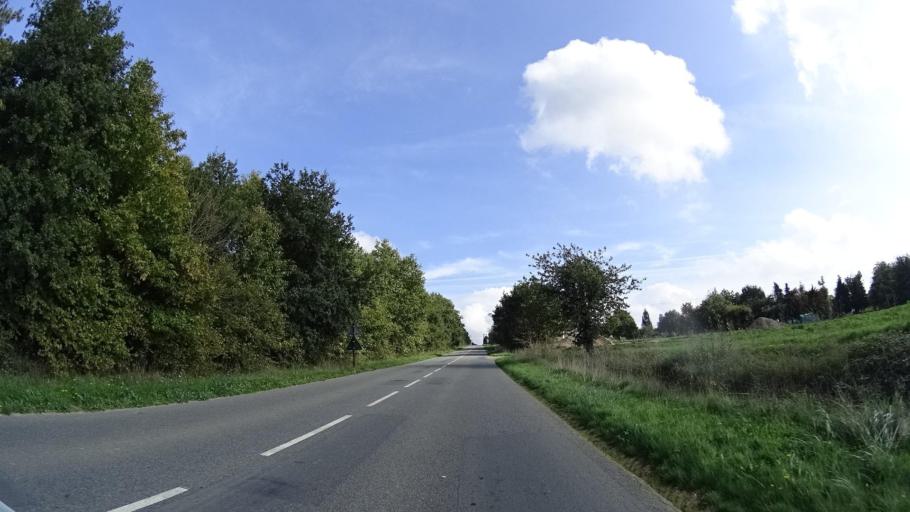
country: FR
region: Brittany
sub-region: Departement des Cotes-d'Armor
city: Plouasne
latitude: 48.2846
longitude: -1.9876
